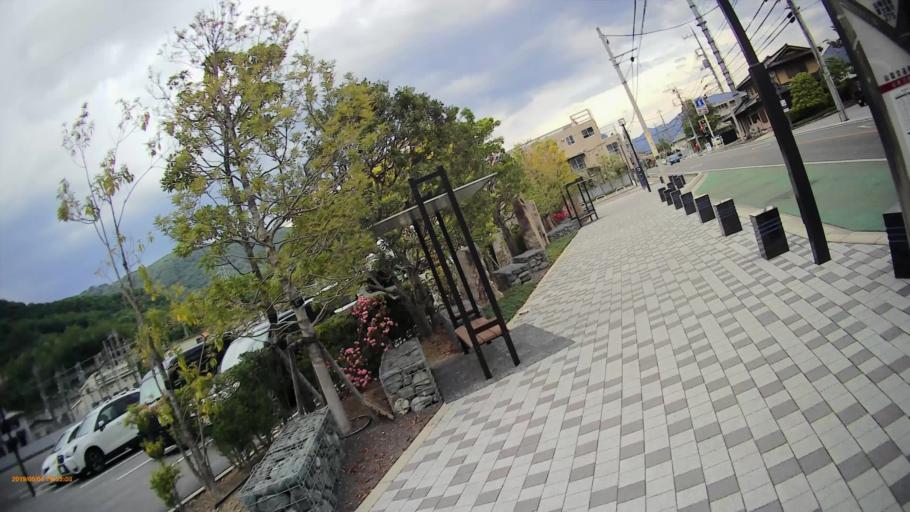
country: JP
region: Yamanashi
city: Isawa
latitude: 35.6579
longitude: 138.6014
